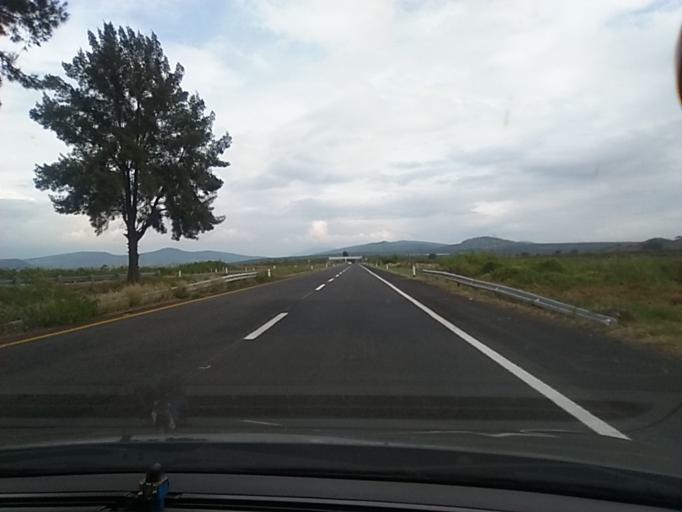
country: MX
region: Michoacan
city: Vistahermosa de Negrete
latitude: 20.2662
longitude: -102.4364
